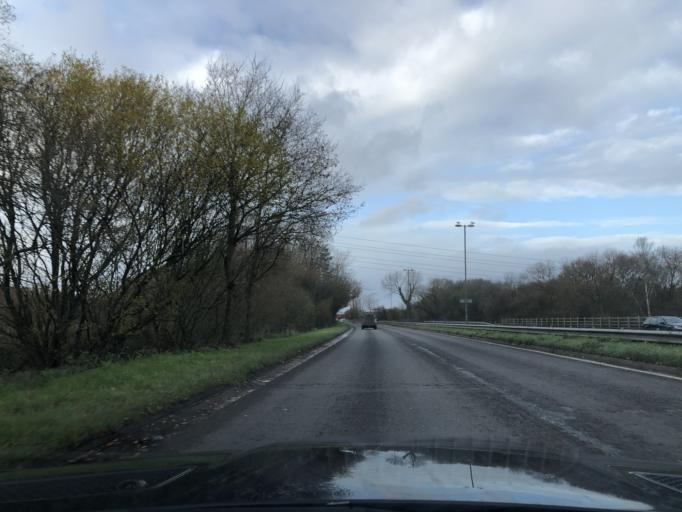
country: GB
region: England
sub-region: Surrey
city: Frimley
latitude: 51.3253
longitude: -0.7662
